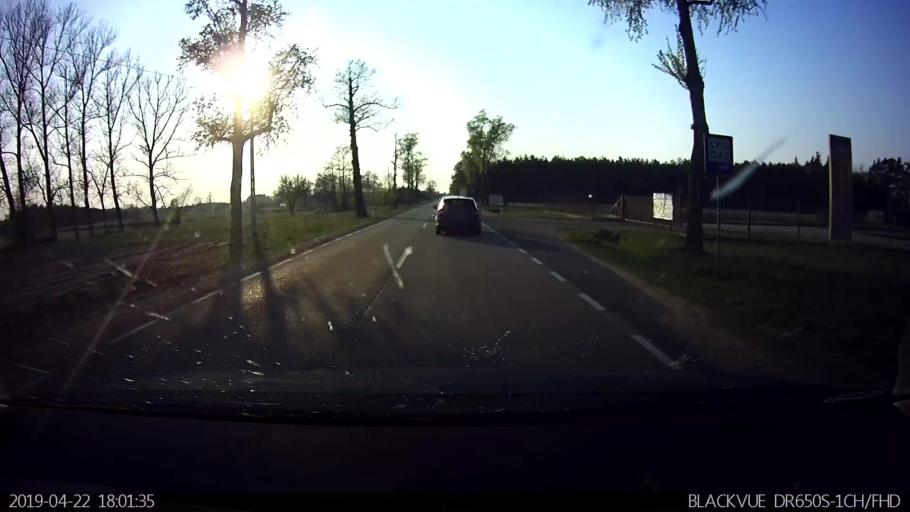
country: PL
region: Masovian Voivodeship
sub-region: Powiat wegrowski
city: Korytnica
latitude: 52.4802
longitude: 21.8263
